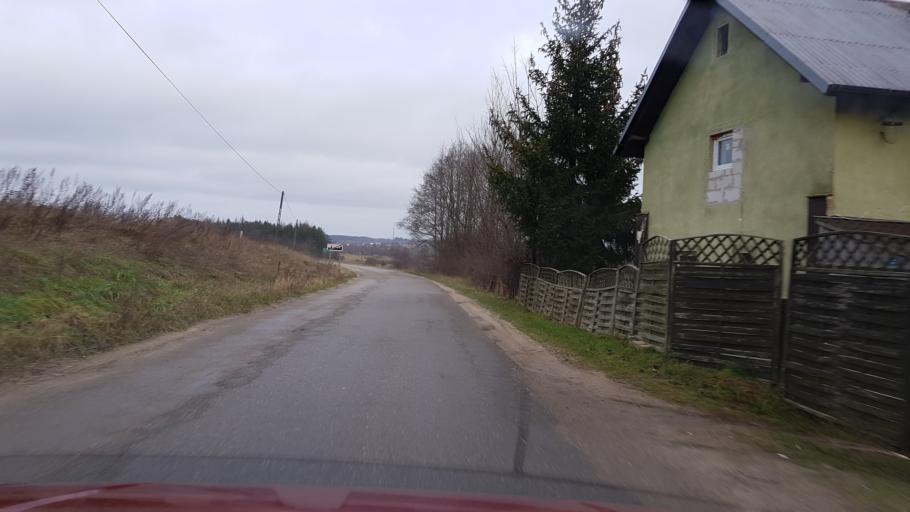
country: PL
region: Pomeranian Voivodeship
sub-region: Powiat bytowski
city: Borzytuchom
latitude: 54.1824
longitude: 17.3640
